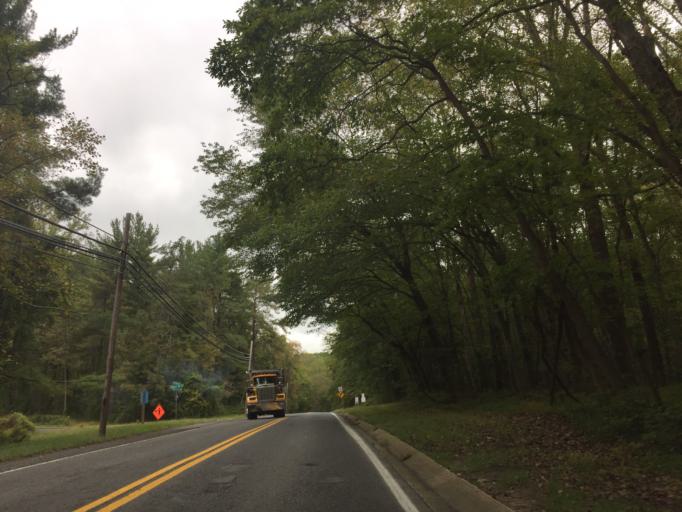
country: US
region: Maryland
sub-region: Baltimore County
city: Hunt Valley
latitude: 39.4923
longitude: -76.6066
